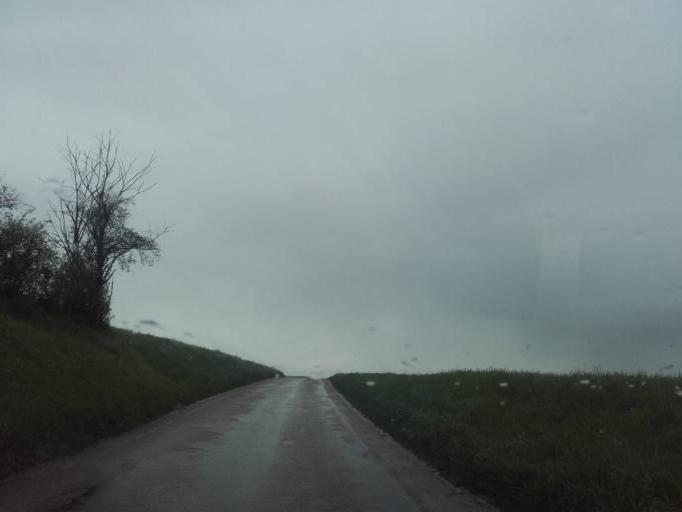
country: FR
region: Bourgogne
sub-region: Departement de l'Yonne
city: Chablis
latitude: 47.8021
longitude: 3.7916
